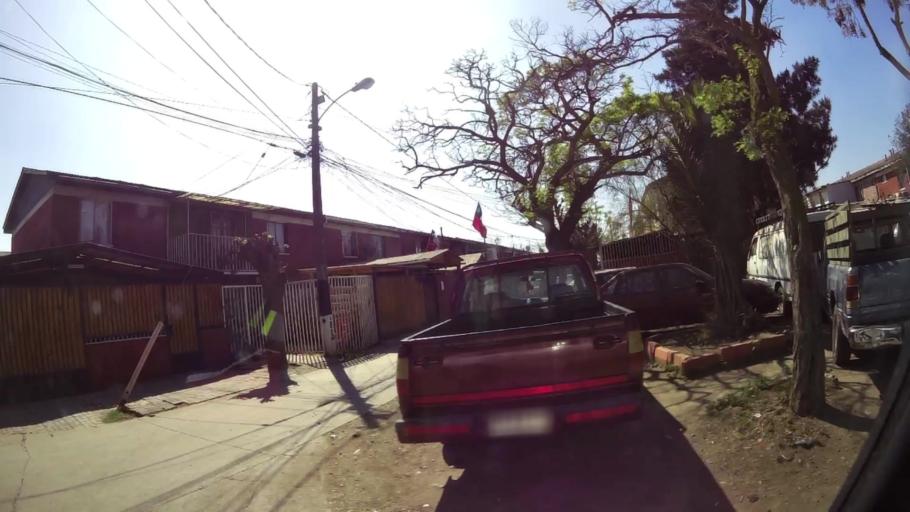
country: CL
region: Santiago Metropolitan
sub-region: Provincia de Santiago
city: Lo Prado
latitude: -33.4980
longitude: -70.7758
